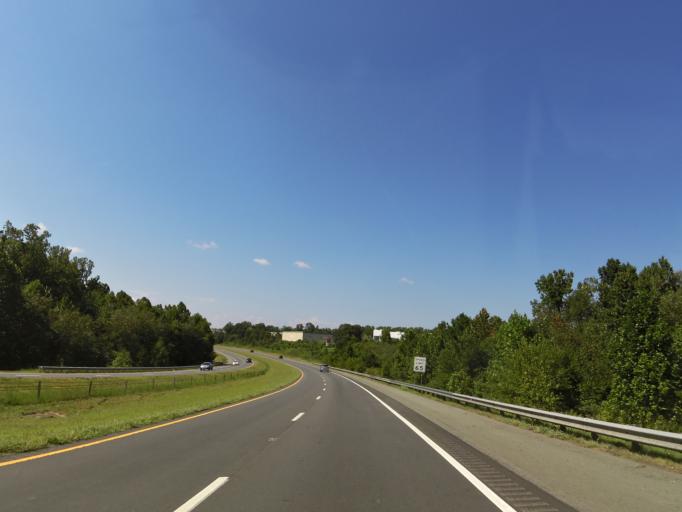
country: US
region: North Carolina
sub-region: Catawba County
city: Maiden
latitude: 35.5367
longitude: -81.2263
